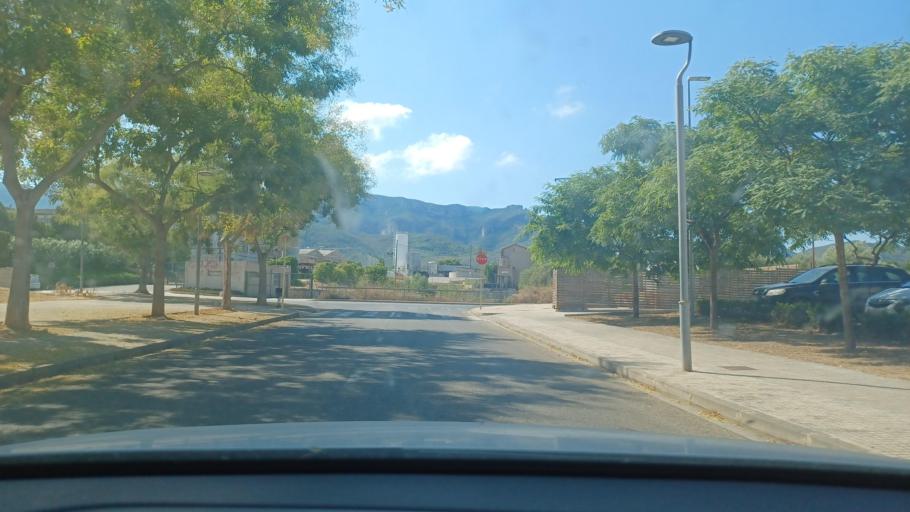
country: ES
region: Catalonia
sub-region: Provincia de Tarragona
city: Sant Carles de la Rapita
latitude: 40.6114
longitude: 0.5833
